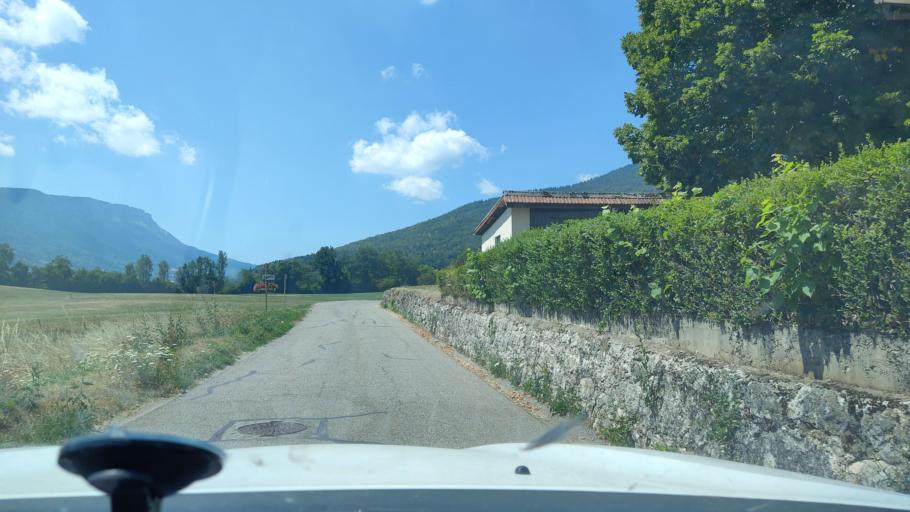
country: FR
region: Rhone-Alpes
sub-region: Departement de la Haute-Savoie
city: Cusy
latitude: 45.7126
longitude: 6.0858
